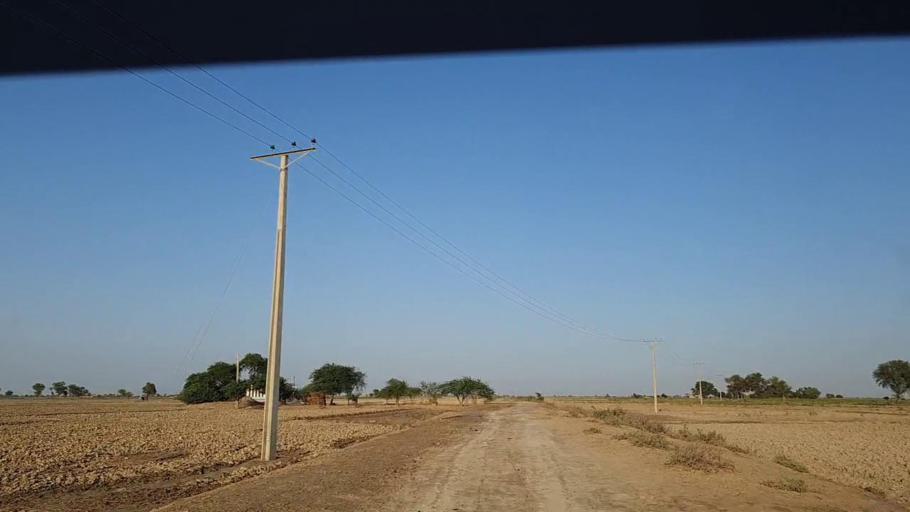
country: PK
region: Sindh
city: Johi
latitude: 26.7443
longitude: 67.6107
